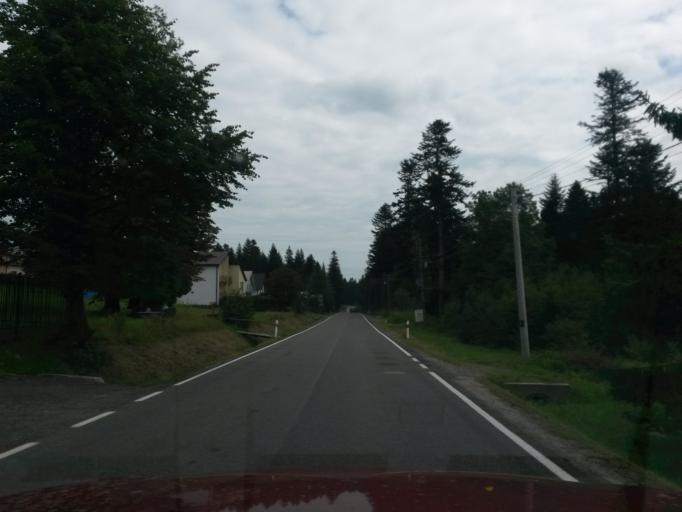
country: PL
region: Lesser Poland Voivodeship
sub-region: Powiat nowosadecki
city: Krynica-Zdroj
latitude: 49.4638
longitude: 20.9564
